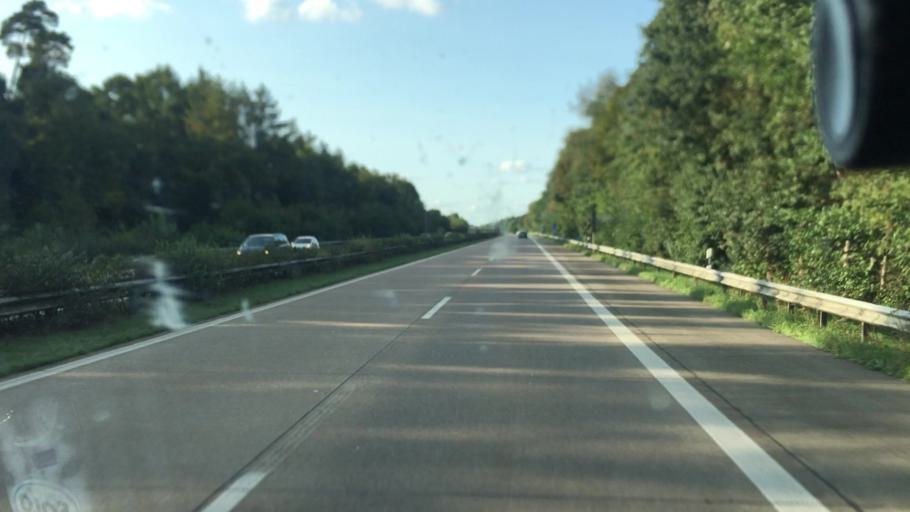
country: DE
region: Lower Saxony
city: Rastede
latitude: 53.2724
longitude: 8.1599
